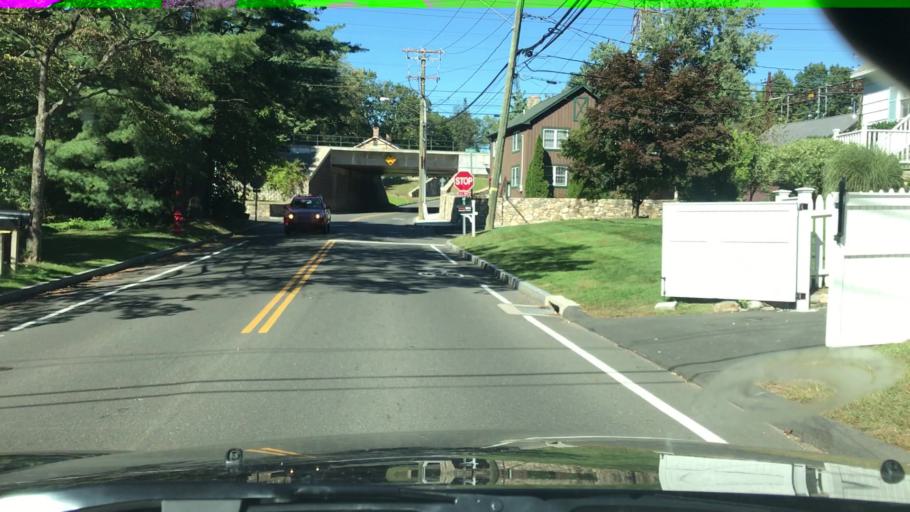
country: US
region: Connecticut
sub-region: Fairfield County
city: Darien
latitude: 41.0766
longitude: -73.4453
